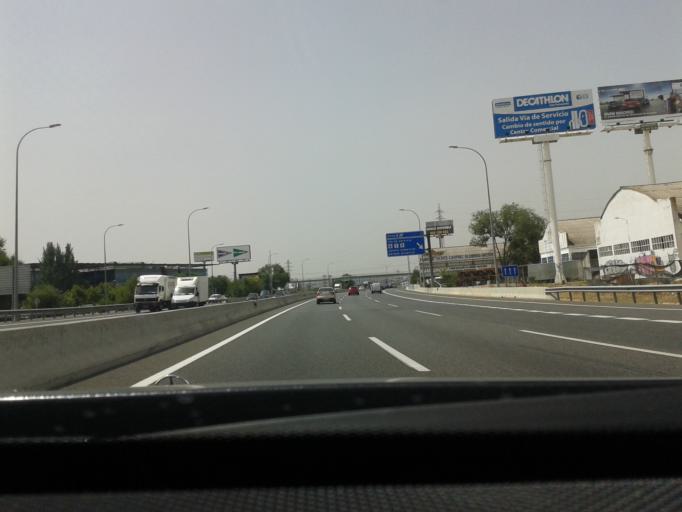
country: ES
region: Madrid
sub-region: Provincia de Madrid
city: San Fernando de Henares
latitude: 40.4542
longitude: -3.5092
